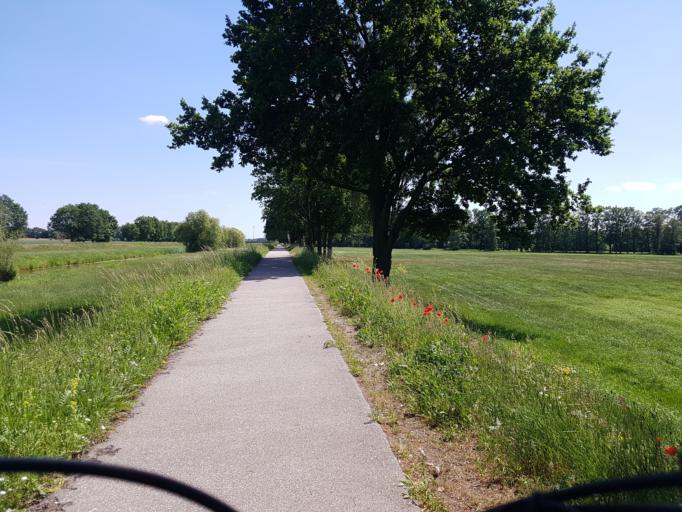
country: DE
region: Brandenburg
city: Elsterwerda
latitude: 51.4725
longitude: 13.4677
